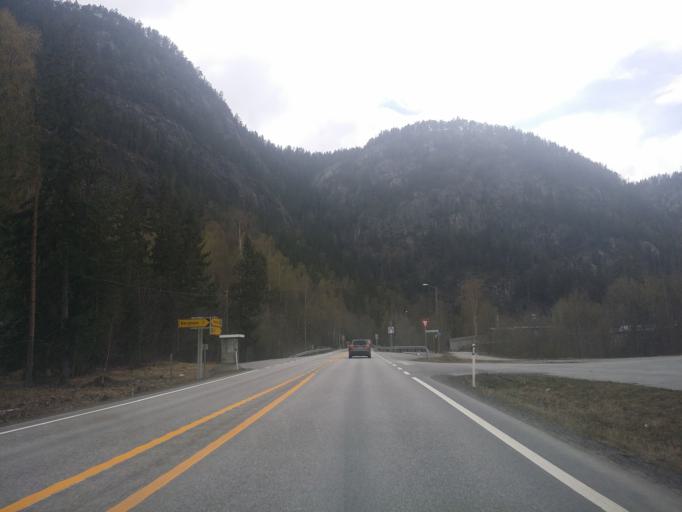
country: NO
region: Buskerud
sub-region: Nes
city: Nesbyen
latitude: 60.4716
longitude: 9.2305
